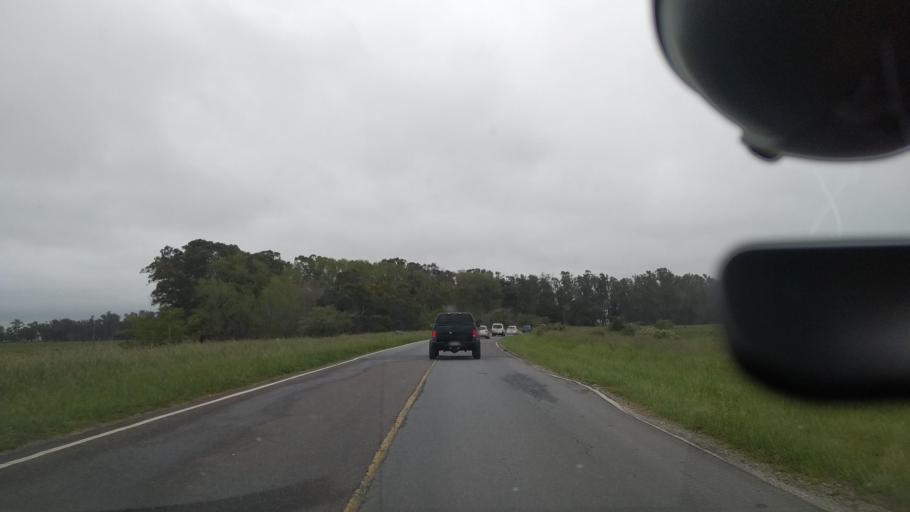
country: AR
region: Buenos Aires
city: Veronica
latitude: -35.5134
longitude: -57.3353
